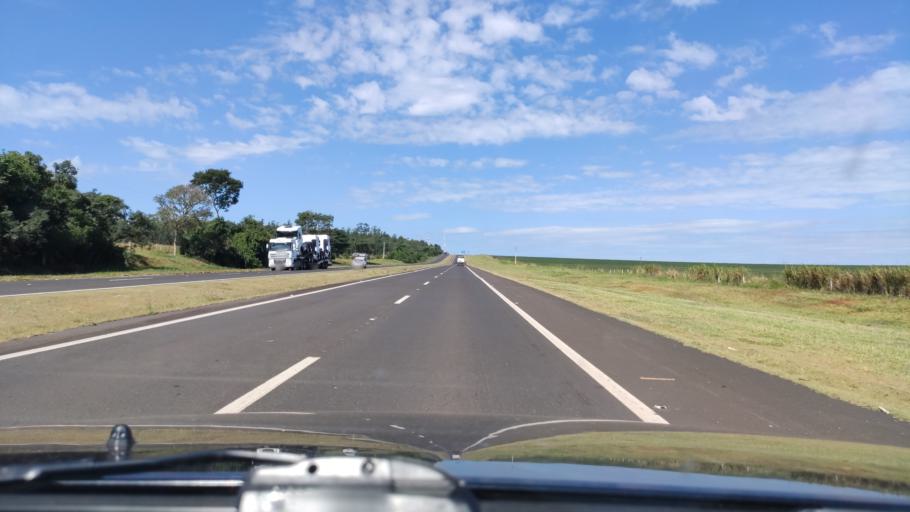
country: BR
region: Sao Paulo
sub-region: Rancharia
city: Rancharia
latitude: -22.4222
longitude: -51.0319
